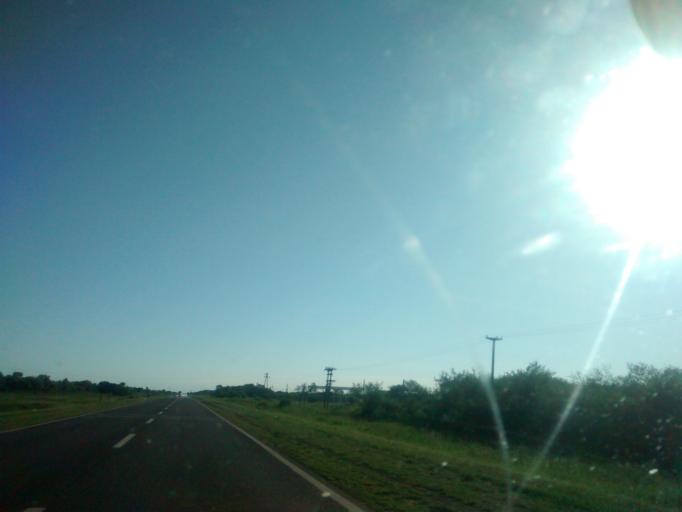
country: AR
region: Chaco
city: Fontana
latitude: -27.4753
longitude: -59.0562
